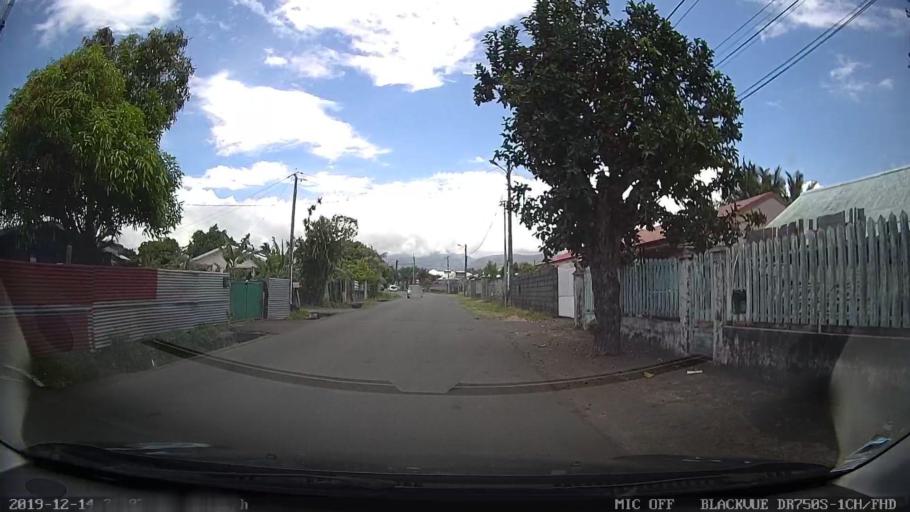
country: RE
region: Reunion
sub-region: Reunion
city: Saint-Andre
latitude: -20.9471
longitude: 55.6634
